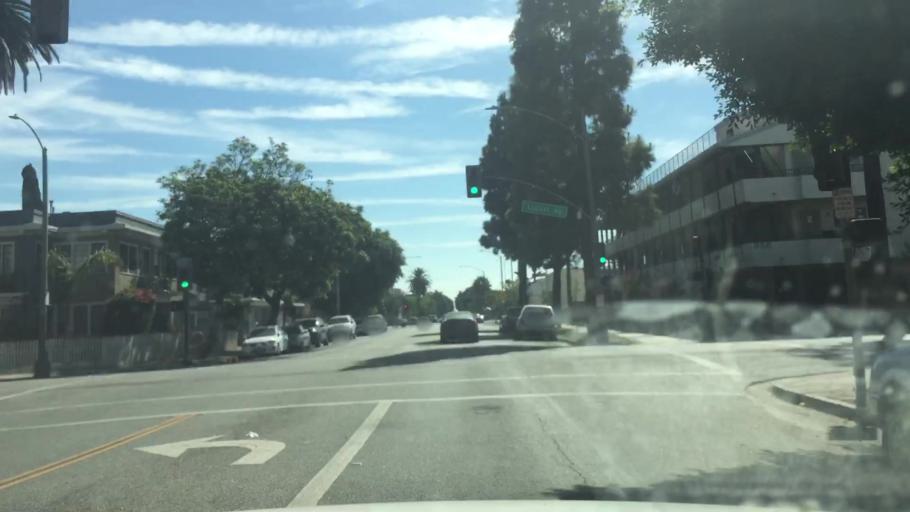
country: US
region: California
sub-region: Los Angeles County
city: Long Beach
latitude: 33.7789
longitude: -118.1914
